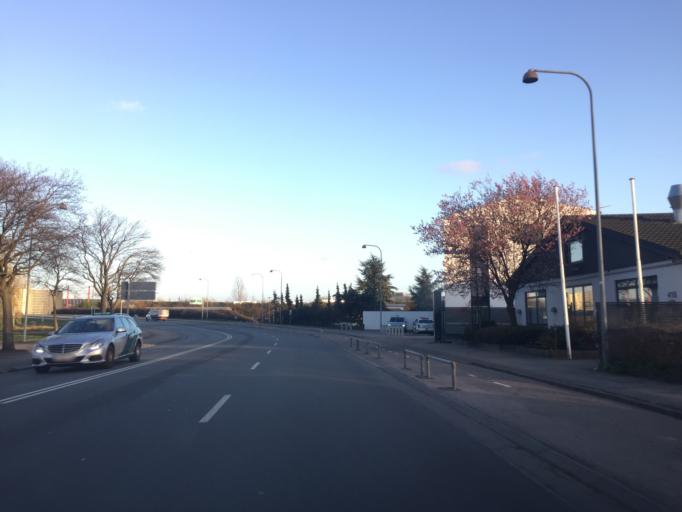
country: DK
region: Capital Region
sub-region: Dragor Kommune
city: Dragor
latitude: 55.6339
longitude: 12.6531
